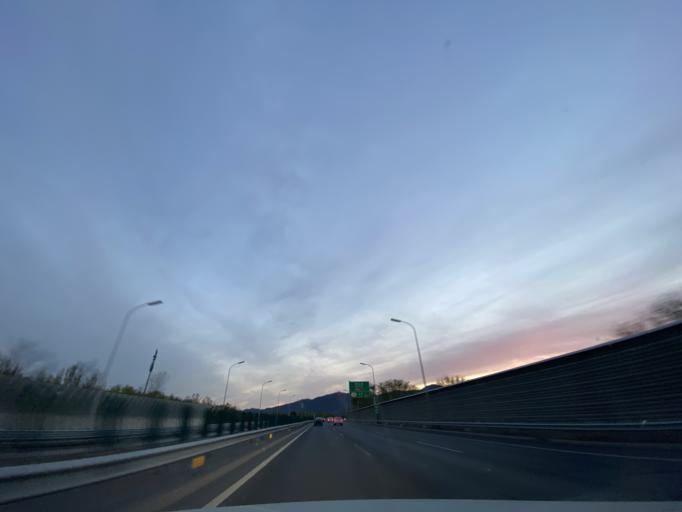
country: CN
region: Beijing
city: Xiangshan
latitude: 39.9987
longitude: 116.2364
